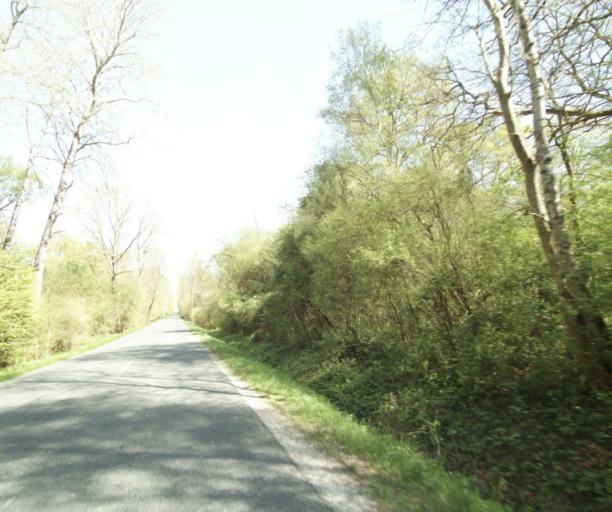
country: FR
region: Ile-de-France
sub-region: Departement de Seine-et-Marne
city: Nangis
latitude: 48.5316
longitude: 2.9813
